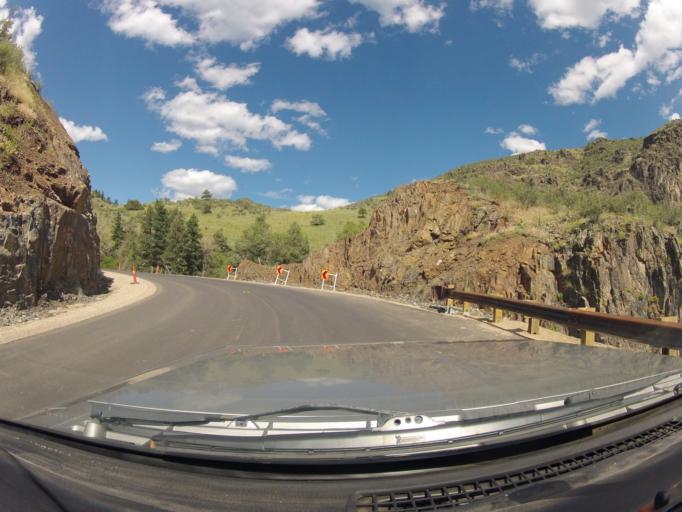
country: US
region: Colorado
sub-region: Larimer County
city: Laporte
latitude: 40.5642
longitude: -105.3048
